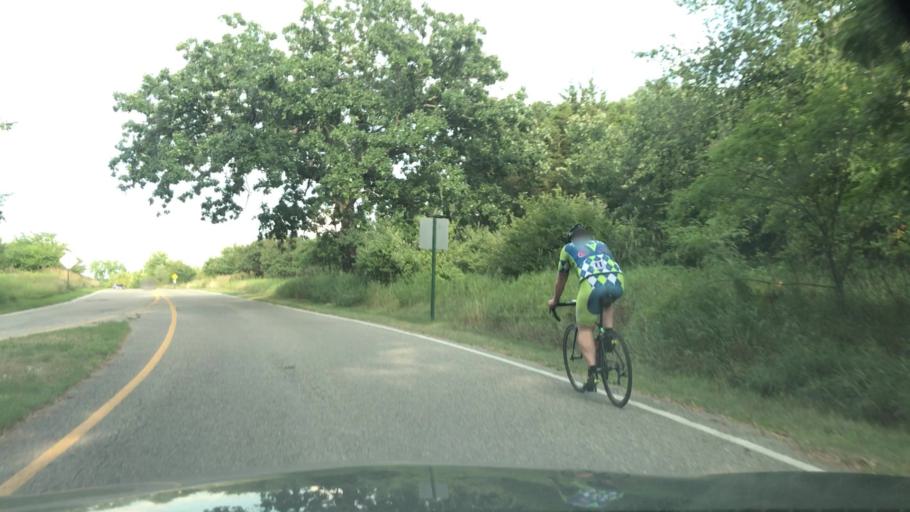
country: US
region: Michigan
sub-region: Oakland County
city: South Lyon
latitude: 42.5106
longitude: -83.6844
